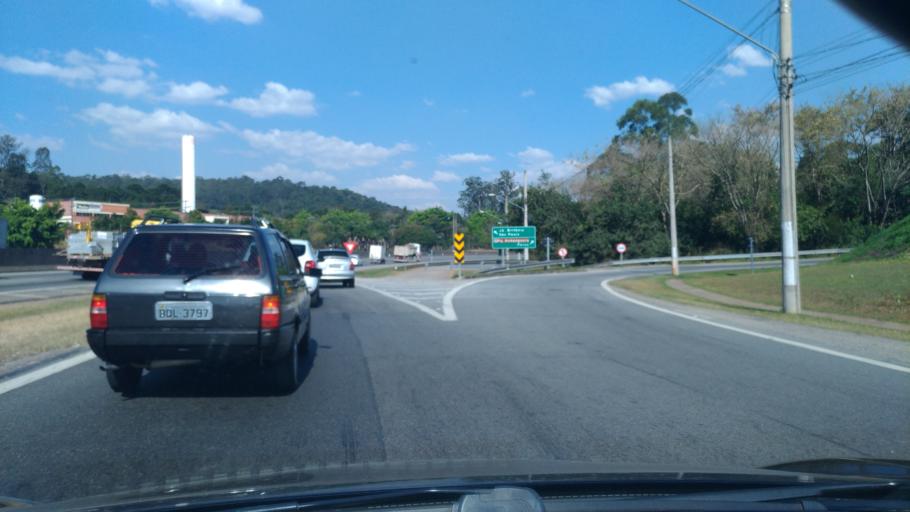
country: BR
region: Sao Paulo
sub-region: Caieiras
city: Caieiras
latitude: -23.4234
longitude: -46.7900
